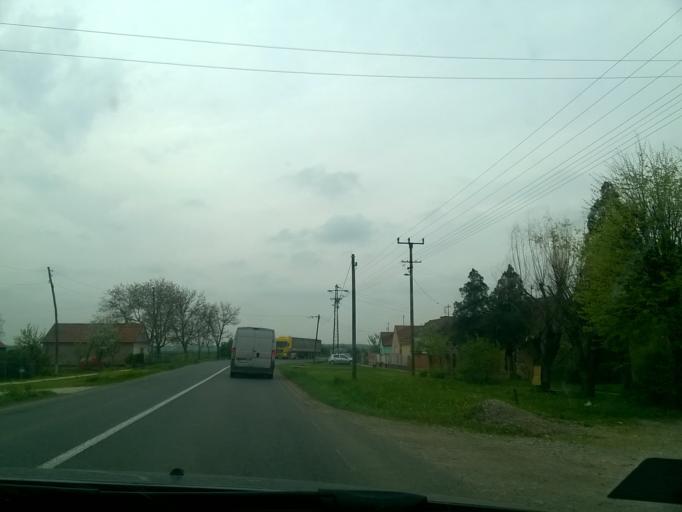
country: RS
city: Platicevo
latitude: 44.8202
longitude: 19.7793
